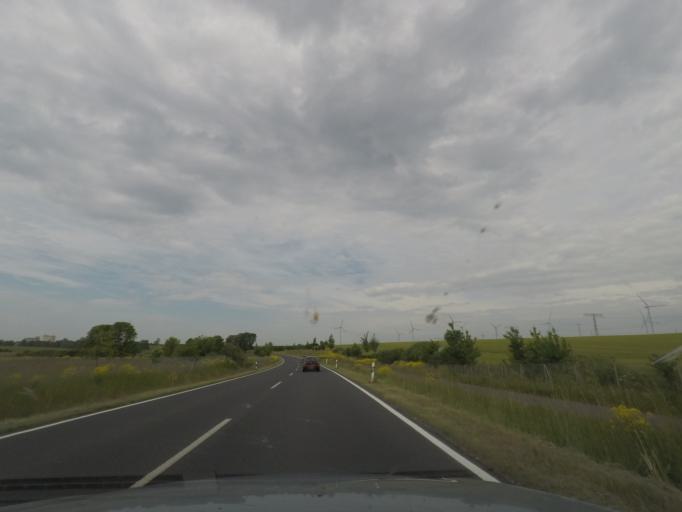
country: DE
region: Brandenburg
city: Grunow
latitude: 53.3377
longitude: 13.9138
